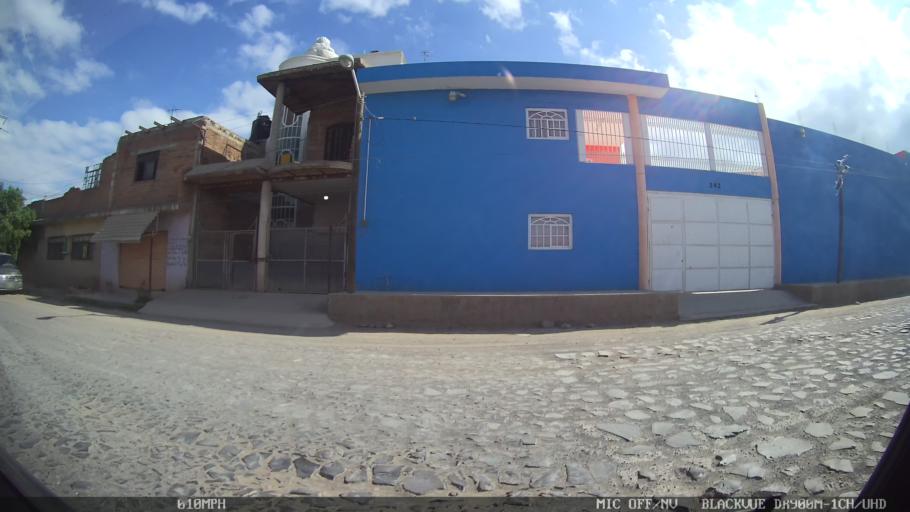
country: MX
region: Jalisco
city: Tonala
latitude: 20.6547
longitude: -103.2463
